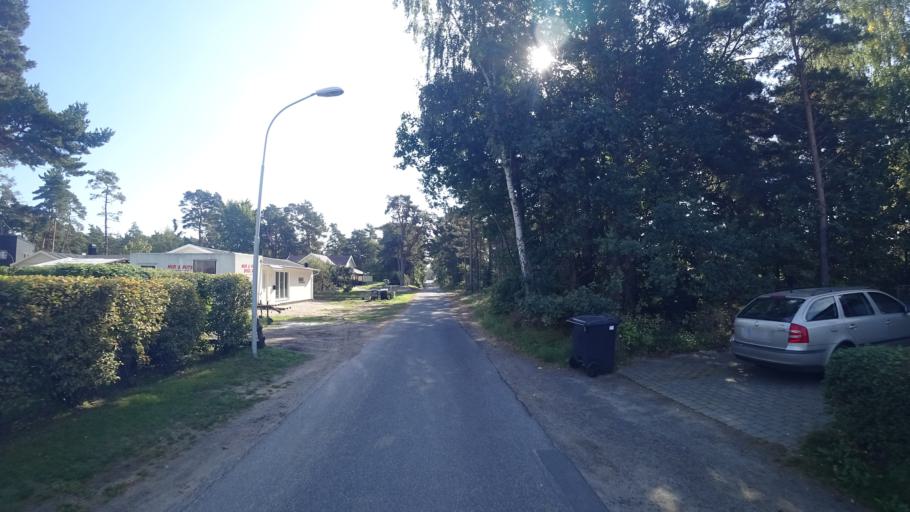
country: SE
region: Skane
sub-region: Kristianstads Kommun
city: Ahus
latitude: 55.9207
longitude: 14.2999
